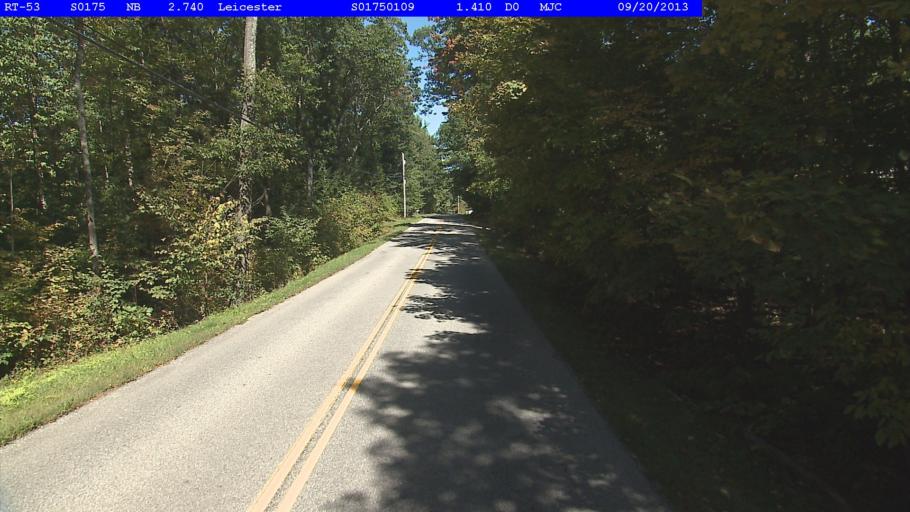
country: US
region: Vermont
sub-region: Rutland County
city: Brandon
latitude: 43.8633
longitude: -73.0668
